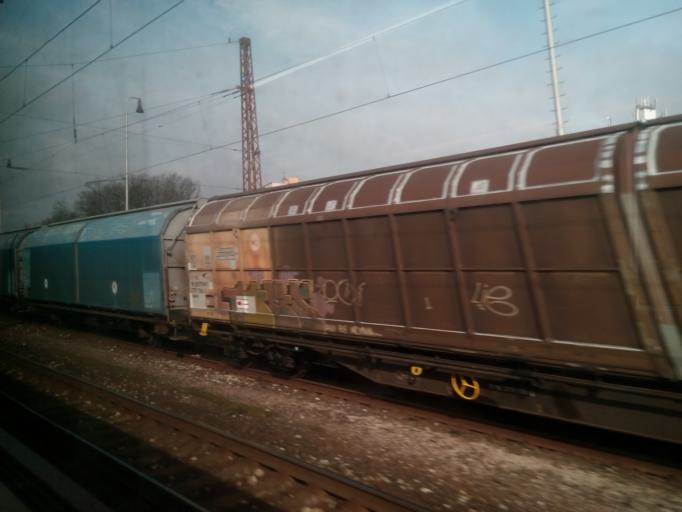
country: SK
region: Zilinsky
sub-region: Okres Zilina
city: Liptovsky Hradok
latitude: 49.0378
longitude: 19.7221
